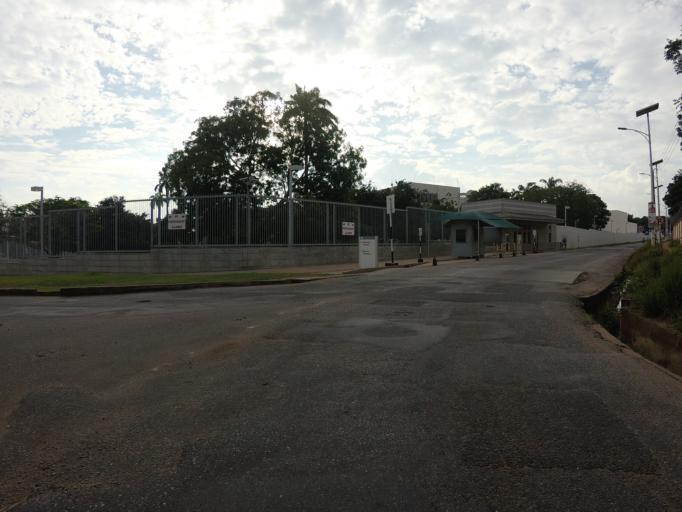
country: GH
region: Greater Accra
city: Accra
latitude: 5.5792
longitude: -0.1691
